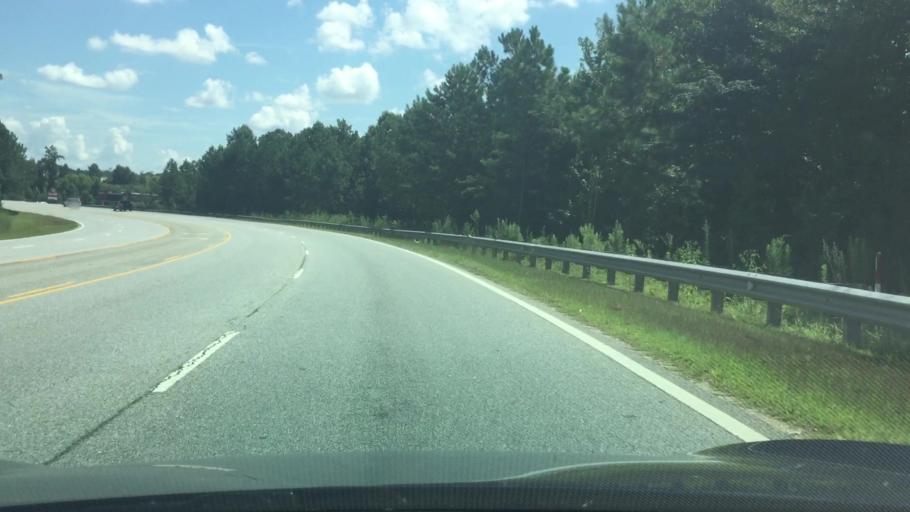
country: US
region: Alabama
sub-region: Lee County
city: Auburn
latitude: 32.6029
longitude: -85.4348
